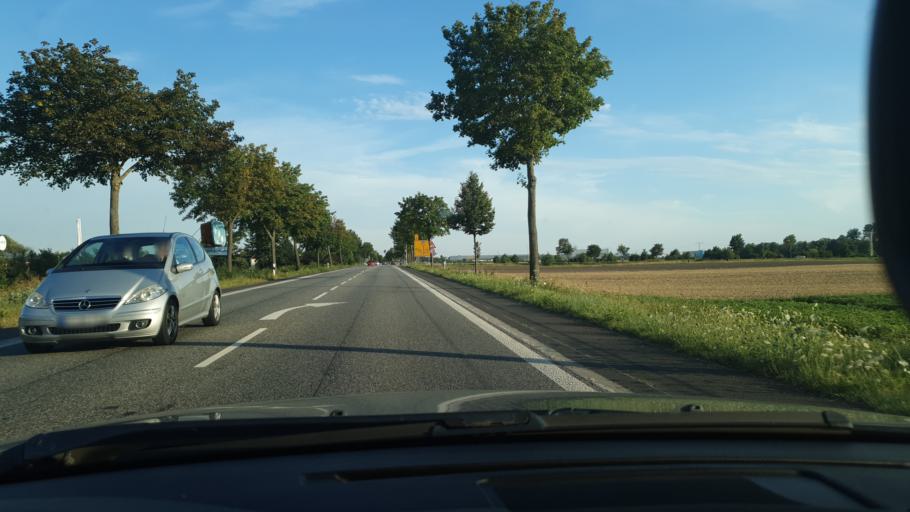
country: DE
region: Rheinland-Pfalz
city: Osthofen
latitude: 49.7087
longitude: 8.3491
